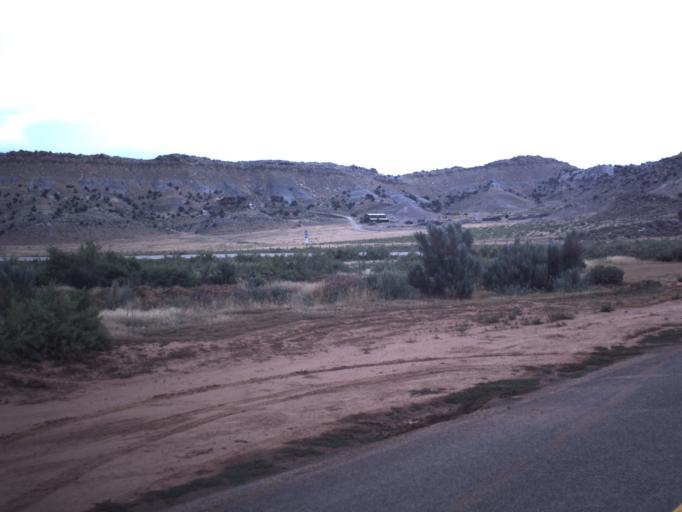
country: US
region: Utah
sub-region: Uintah County
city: Vernal
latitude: 40.5337
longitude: -109.5233
